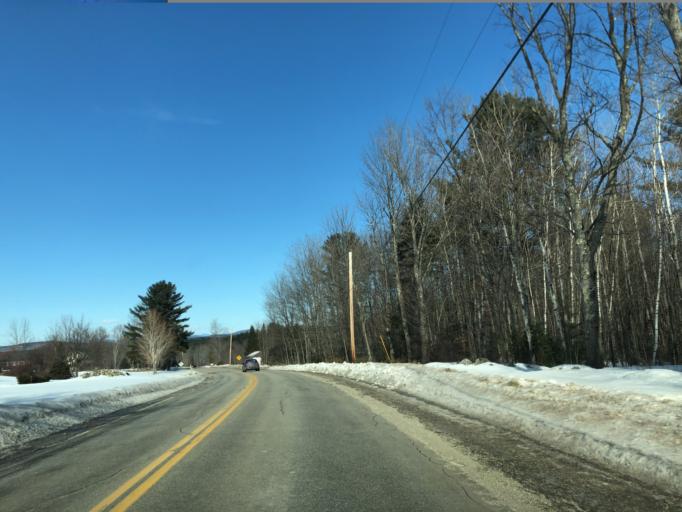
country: US
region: Maine
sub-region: Oxford County
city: Hebron
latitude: 44.2105
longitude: -70.3422
